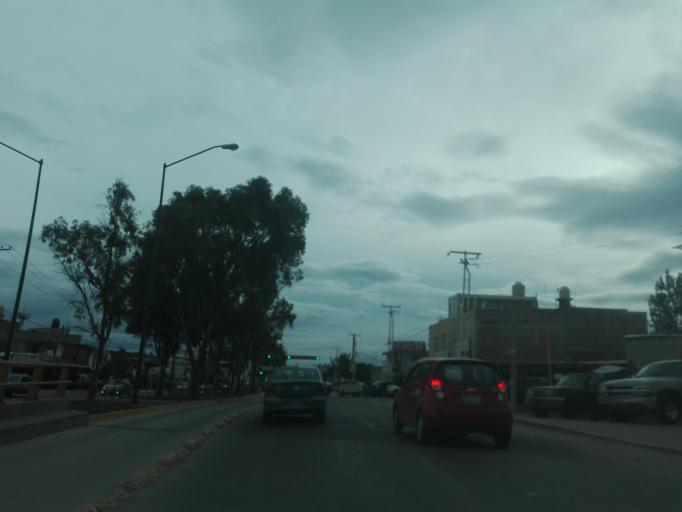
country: MX
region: Guanajuato
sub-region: Leon
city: Medina
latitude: 21.1352
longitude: -101.6431
